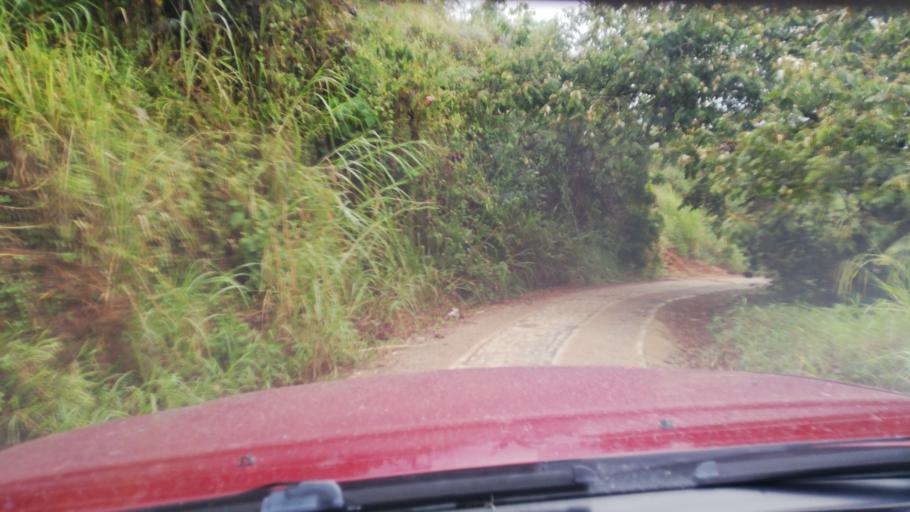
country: CO
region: Risaralda
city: Balboa
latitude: 4.8862
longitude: -75.9689
